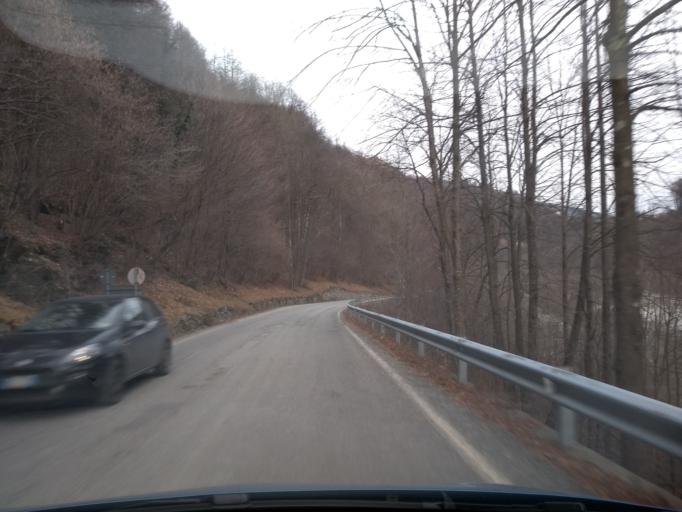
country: IT
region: Piedmont
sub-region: Provincia di Torino
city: Viu
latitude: 45.2312
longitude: 7.3516
